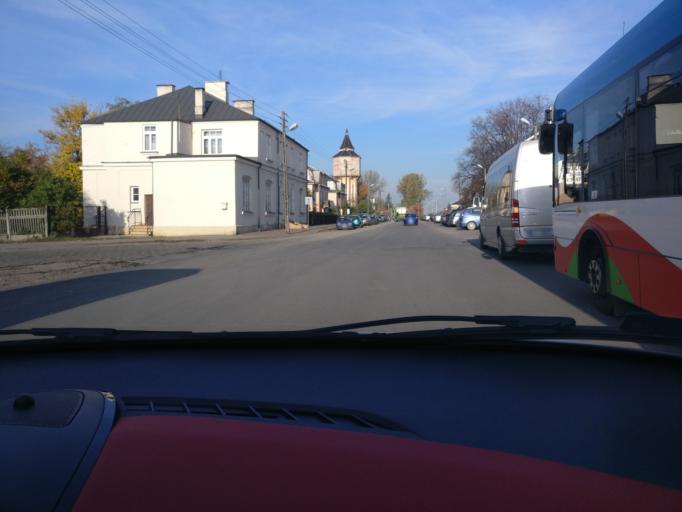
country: PL
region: Lublin Voivodeship
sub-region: Powiat rycki
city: Deblin
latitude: 51.5772
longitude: 21.8350
